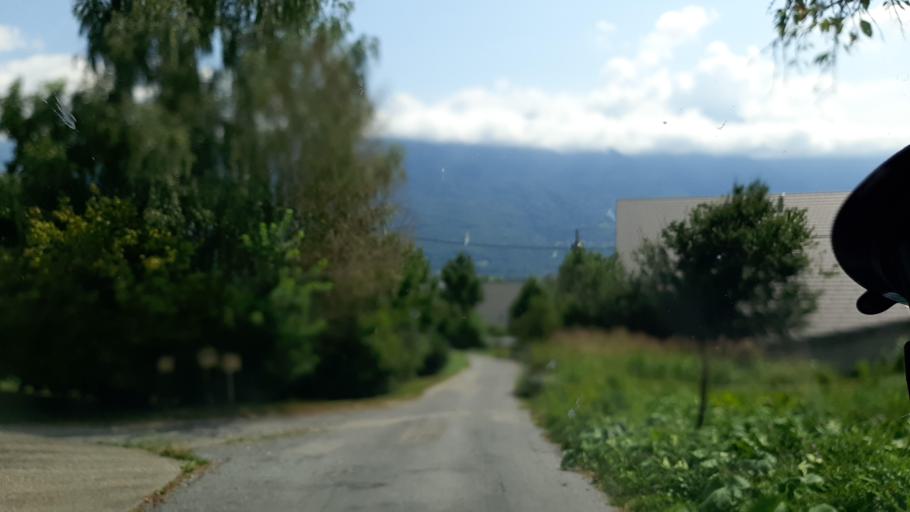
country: FR
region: Rhone-Alpes
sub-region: Departement de la Savoie
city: Mercury
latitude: 45.6777
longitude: 6.3359
